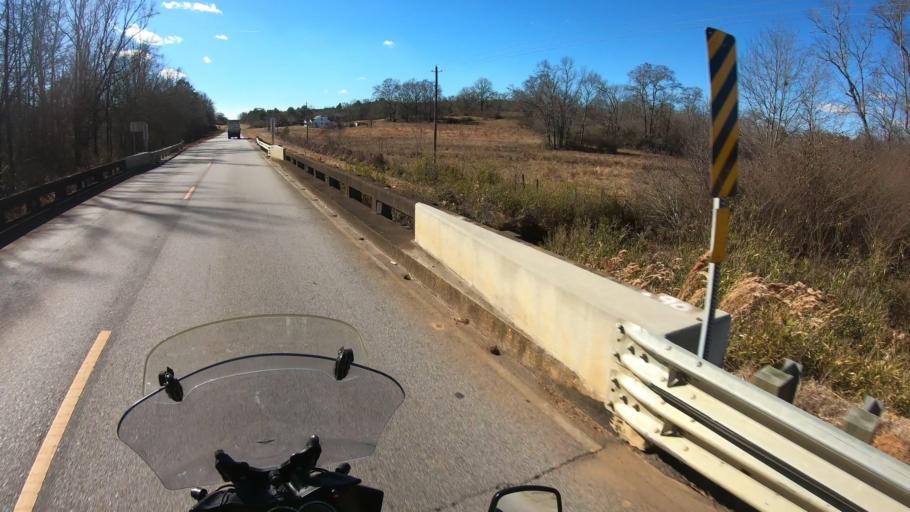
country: US
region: Alabama
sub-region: Clay County
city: Lineville
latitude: 33.4775
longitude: -85.6919
